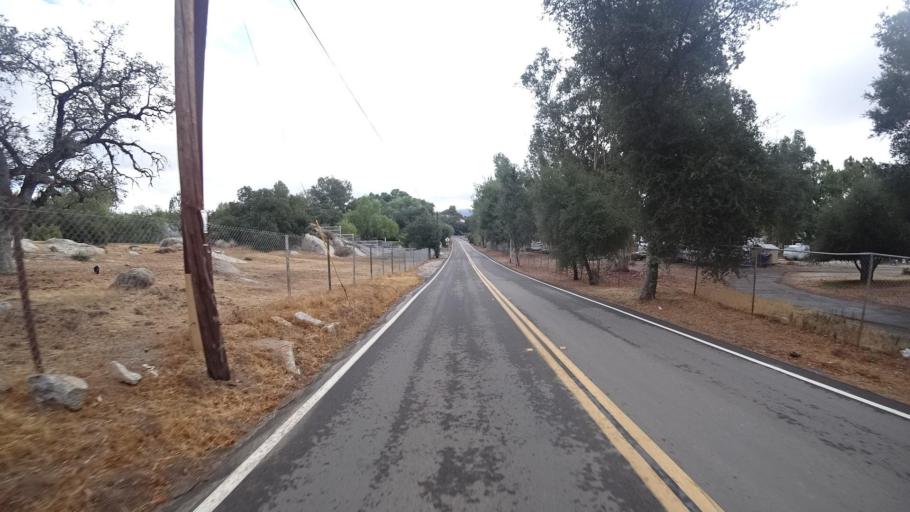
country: MX
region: Baja California
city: Tecate
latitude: 32.6259
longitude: -116.6118
